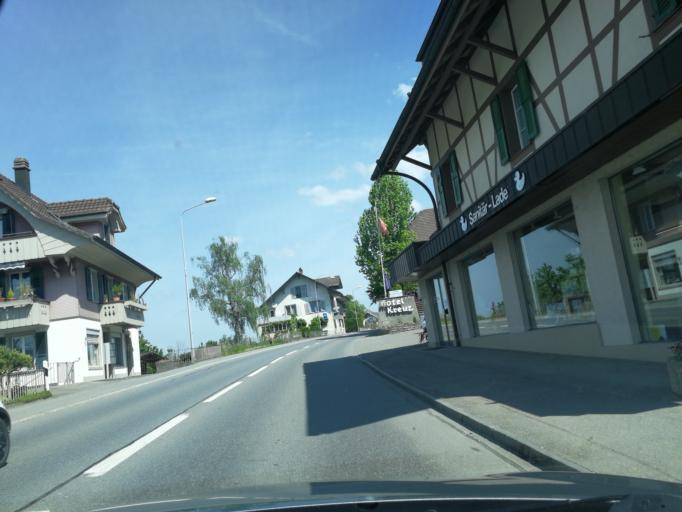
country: CH
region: Bern
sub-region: Bern-Mittelland District
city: Niederwichtrach
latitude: 46.8434
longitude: 7.5765
